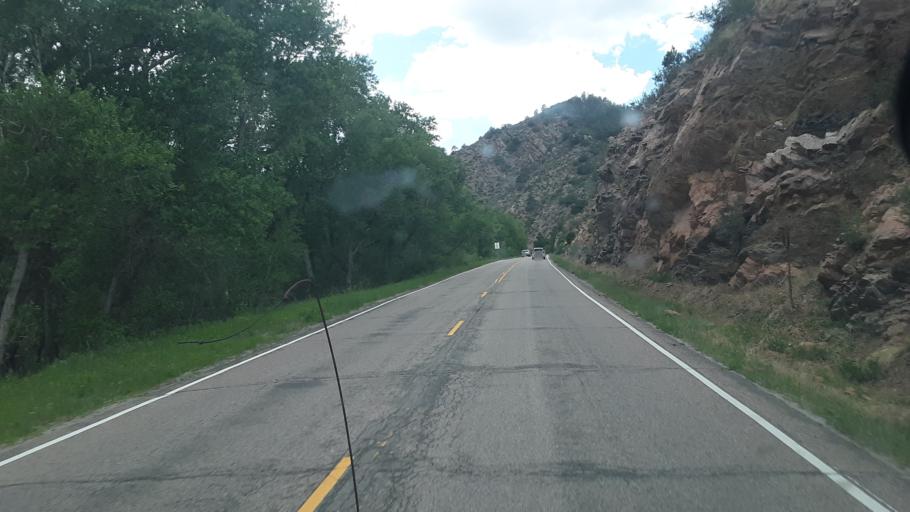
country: US
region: Colorado
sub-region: Fremont County
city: Florence
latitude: 38.1764
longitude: -105.1363
